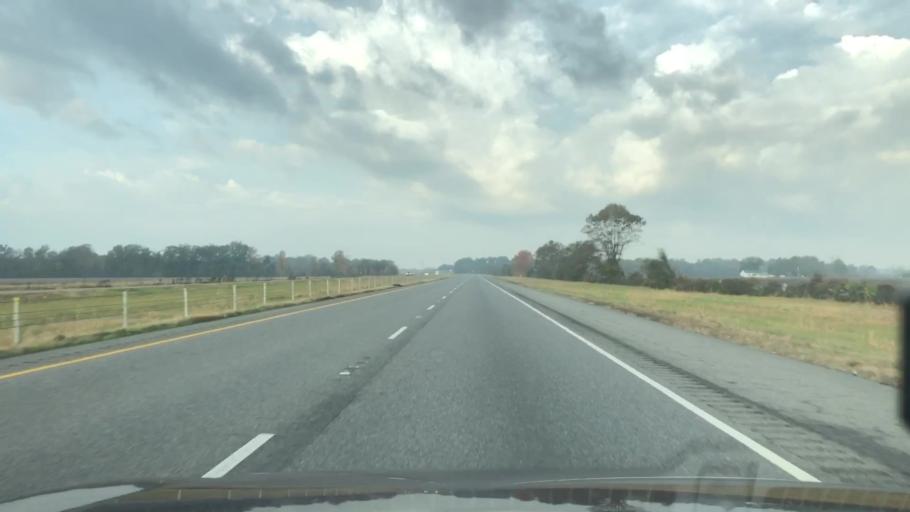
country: US
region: Louisiana
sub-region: Madison Parish
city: Tallulah
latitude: 32.4175
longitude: -91.2856
